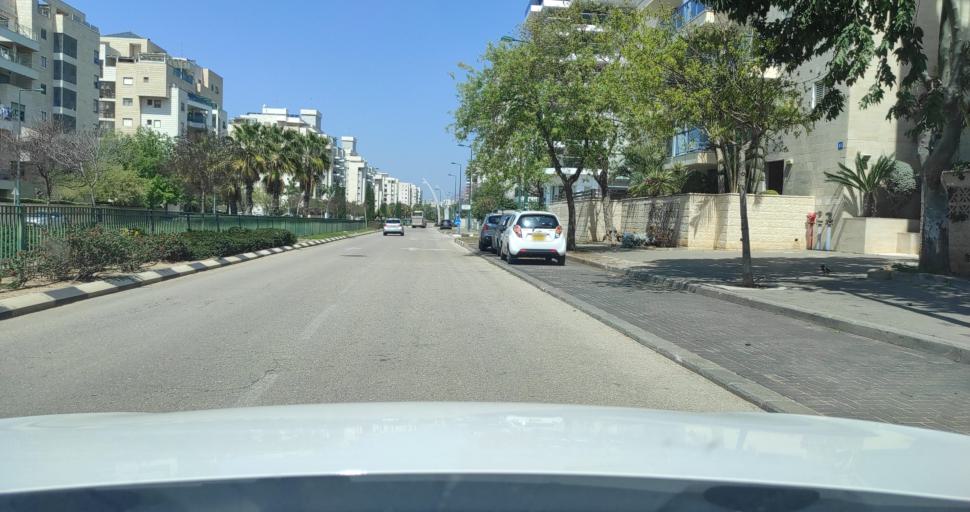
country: IL
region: Central District
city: Nordiyya
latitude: 32.2961
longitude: 34.8735
